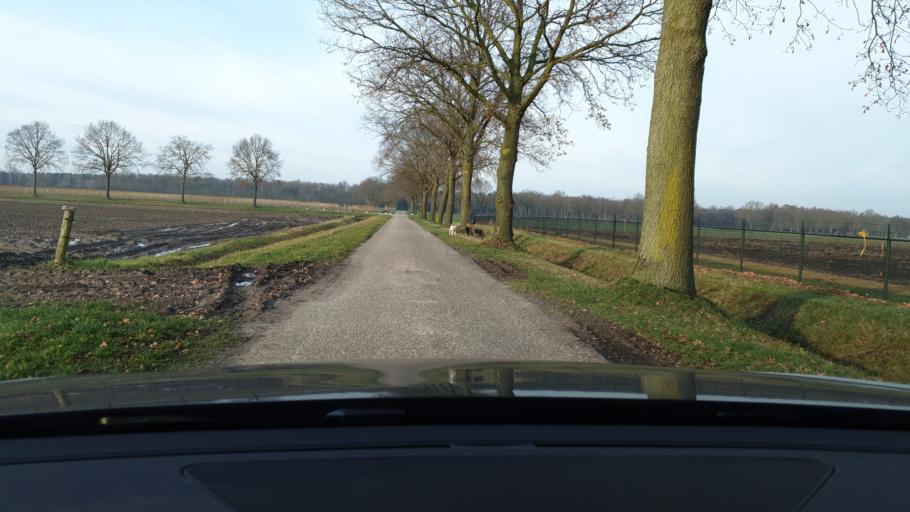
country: NL
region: Limburg
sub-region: Gemeente Venray
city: Venray
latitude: 51.4703
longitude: 6.0325
